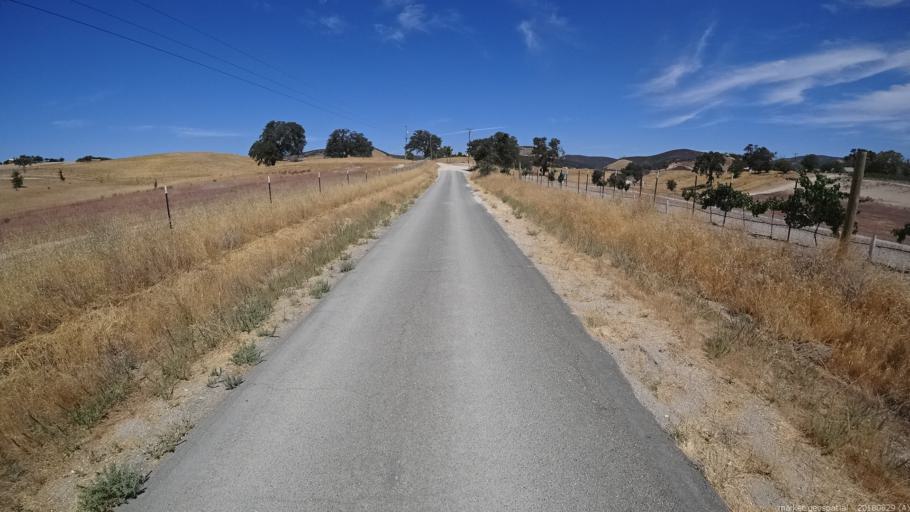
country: US
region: California
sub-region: Monterey County
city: King City
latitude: 35.9503
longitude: -121.0642
